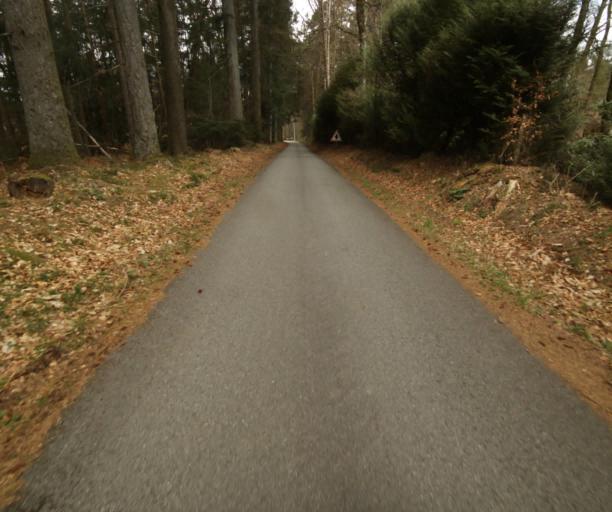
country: FR
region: Limousin
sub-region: Departement de la Correze
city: Correze
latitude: 45.3363
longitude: 1.9508
